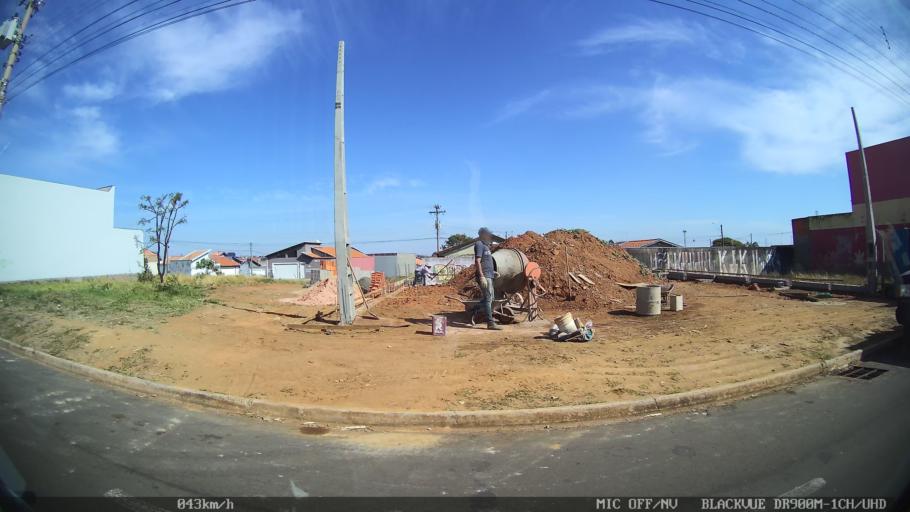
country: BR
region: Sao Paulo
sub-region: Franca
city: Franca
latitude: -20.4794
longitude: -47.4080
